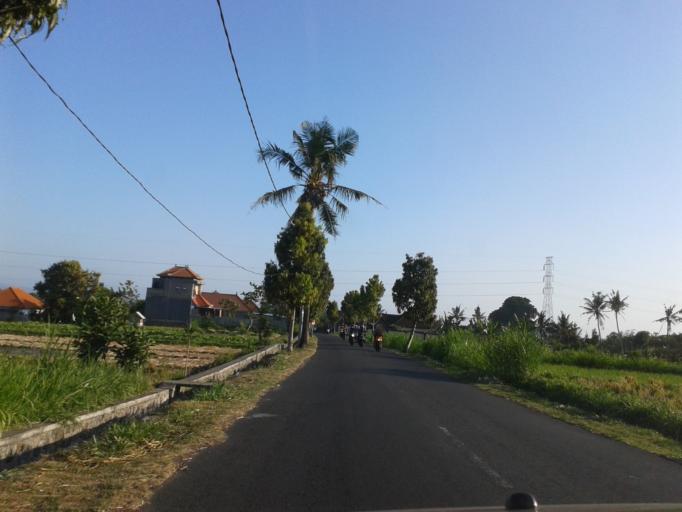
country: ID
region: Bali
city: Semarapura
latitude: -8.5607
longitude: 115.3866
